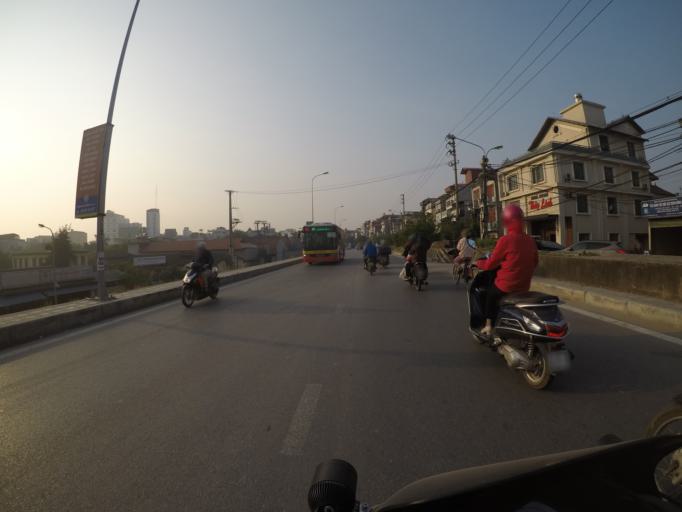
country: VN
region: Ha Noi
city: Hoan Kiem
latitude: 21.0423
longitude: 105.8653
